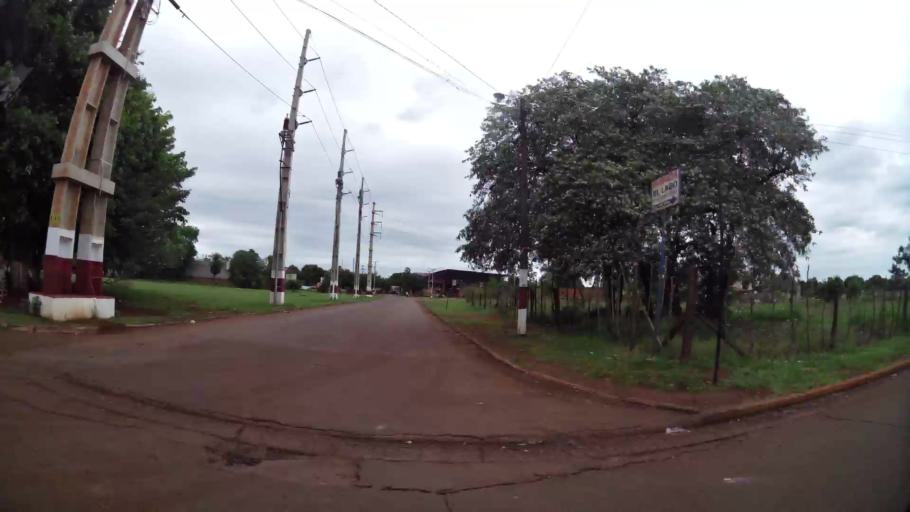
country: PY
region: Alto Parana
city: Ciudad del Este
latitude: -25.4056
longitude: -54.6281
